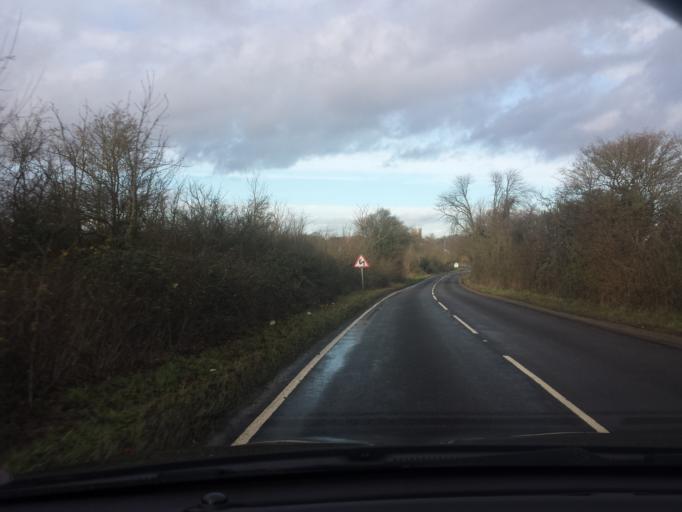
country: GB
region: England
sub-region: Essex
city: Alresford
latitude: 51.8909
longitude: 1.0283
